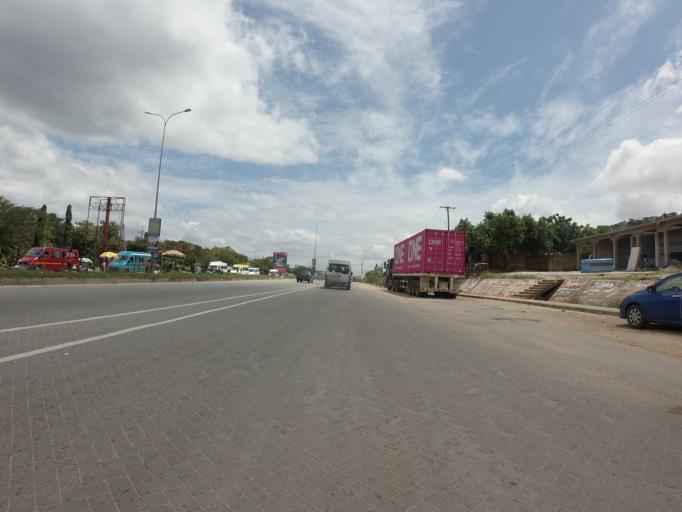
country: GH
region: Central
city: Kasoa
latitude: 5.5477
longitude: -0.3802
